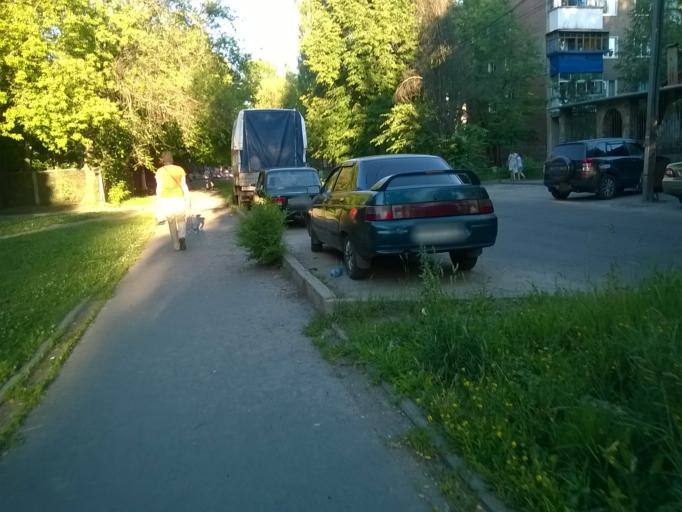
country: RU
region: Kursk
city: Kursk
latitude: 51.6698
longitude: 36.1483
